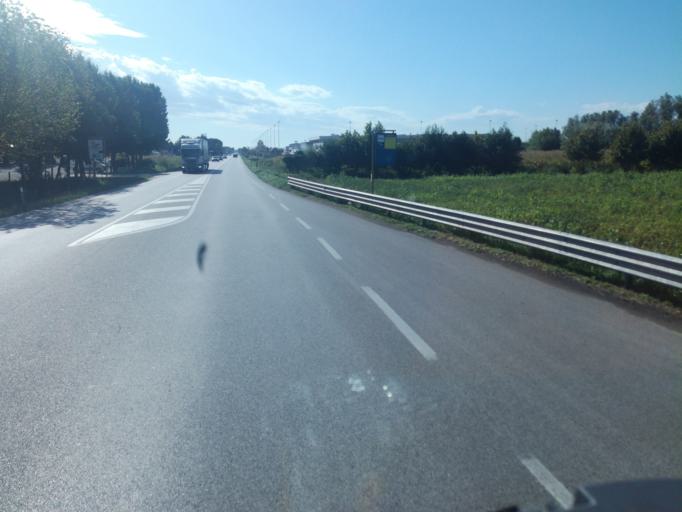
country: IT
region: Veneto
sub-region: Provincia di Padova
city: Corte
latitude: 45.2917
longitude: 12.0619
